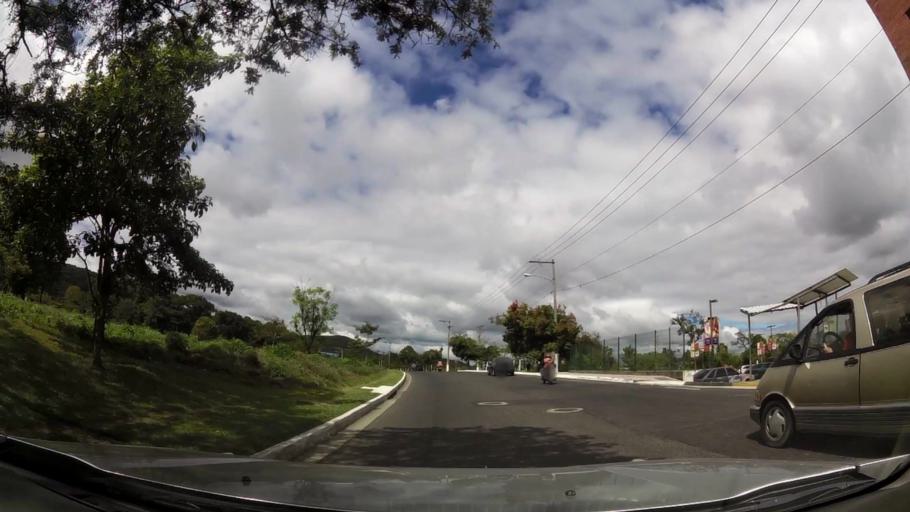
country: GT
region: Guatemala
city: Guatemala City
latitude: 14.6543
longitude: -90.5404
